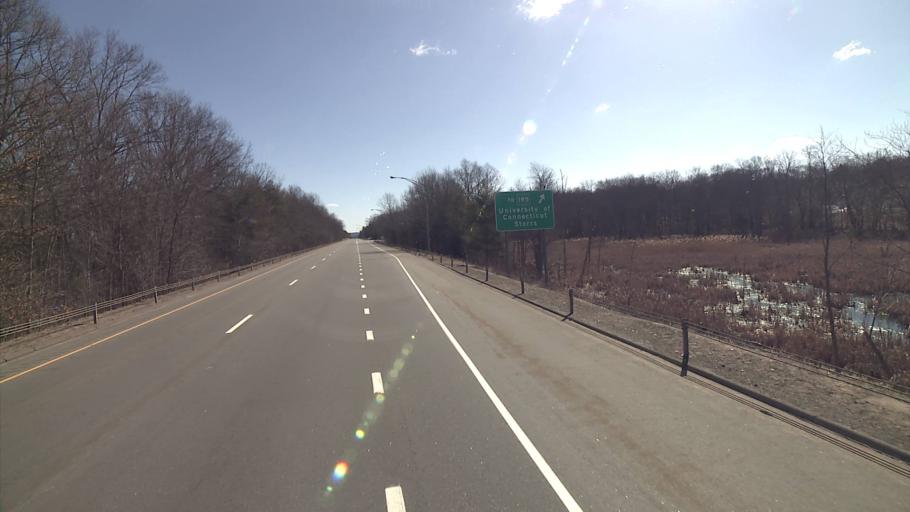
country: US
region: Connecticut
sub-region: Windham County
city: Willimantic
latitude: 41.7294
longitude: -72.2225
